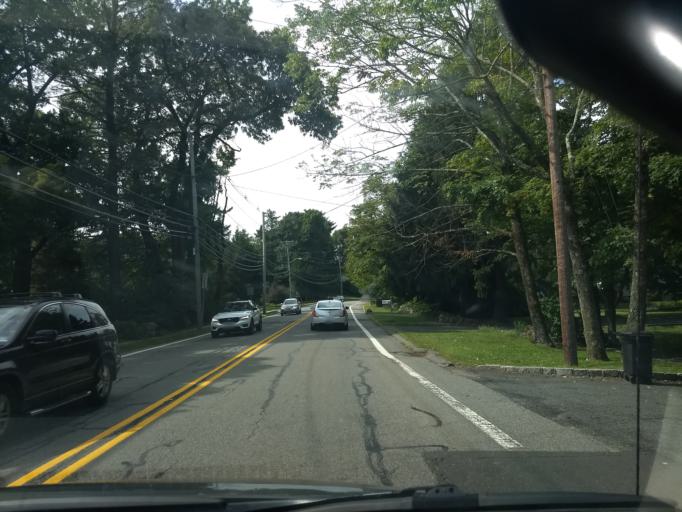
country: US
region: New Jersey
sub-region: Morris County
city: Morris Plains
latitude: 40.8310
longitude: -74.4755
